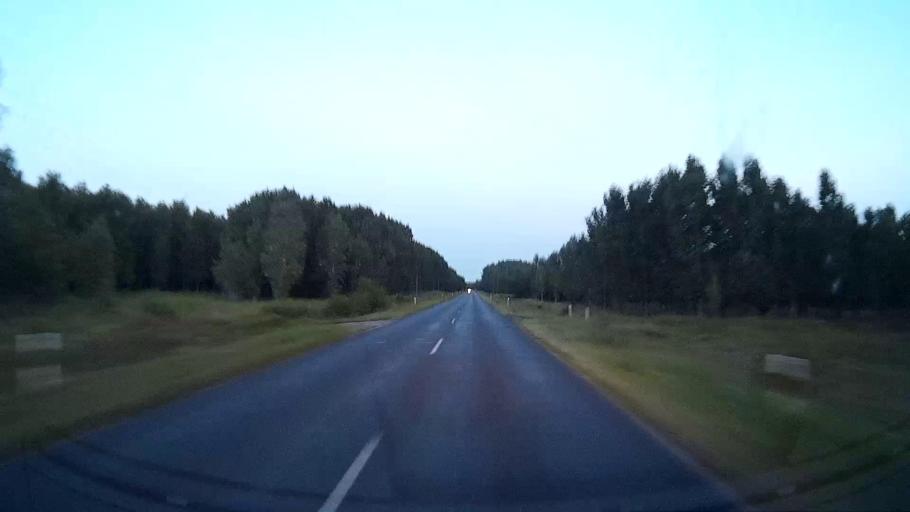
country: HU
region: Pest
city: Cegledbercel
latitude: 47.2006
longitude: 19.7046
